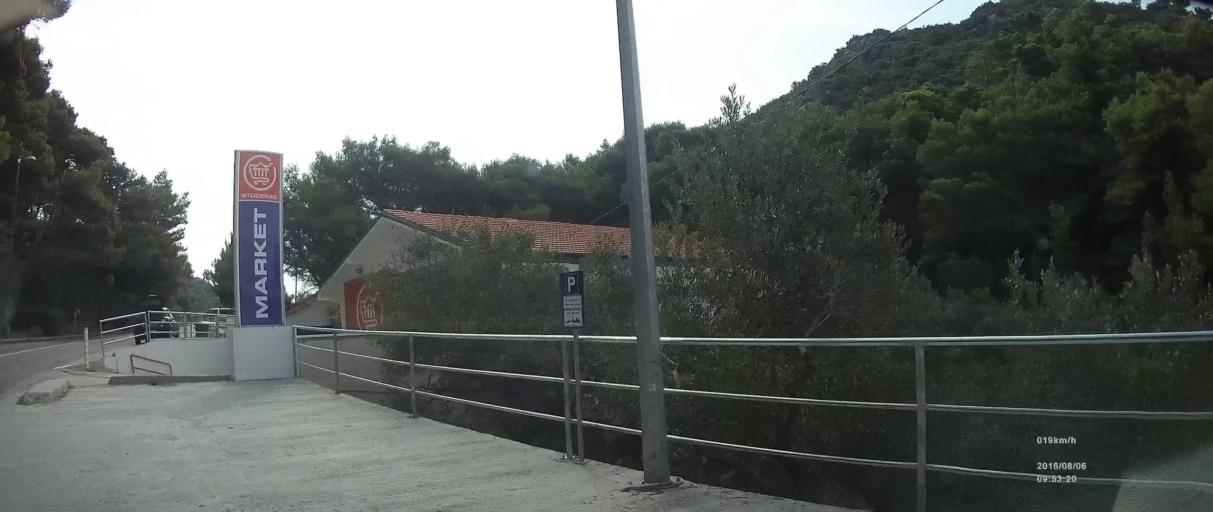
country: HR
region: Dubrovacko-Neretvanska
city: Blato
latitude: 42.7320
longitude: 17.5835
